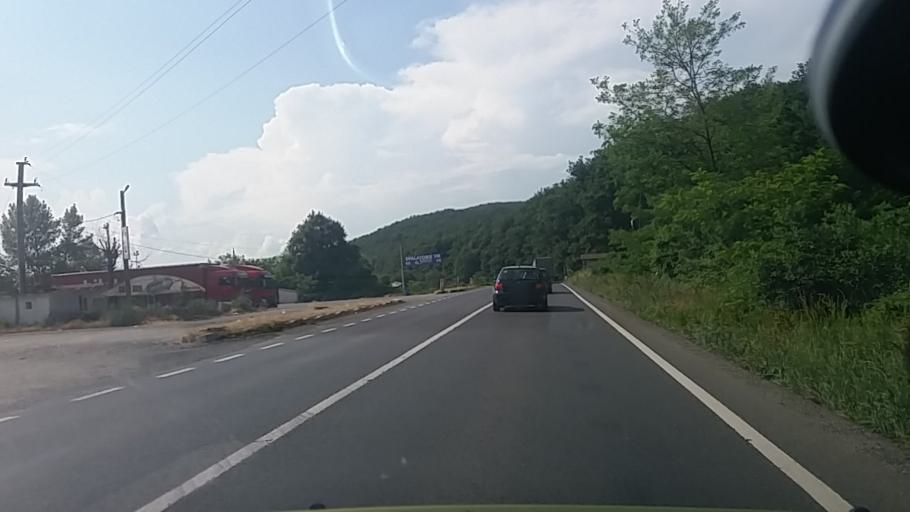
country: RO
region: Arad
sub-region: Comuna Bata
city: Bata
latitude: 46.0706
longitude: 22.0391
